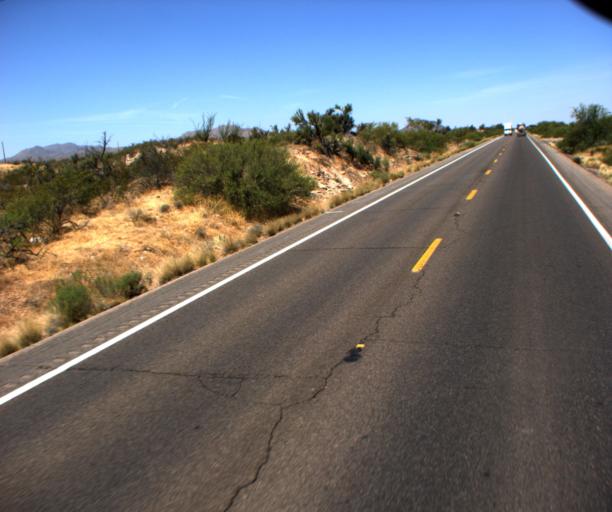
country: US
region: Arizona
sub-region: Gila County
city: Peridot
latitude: 33.3067
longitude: -110.4903
